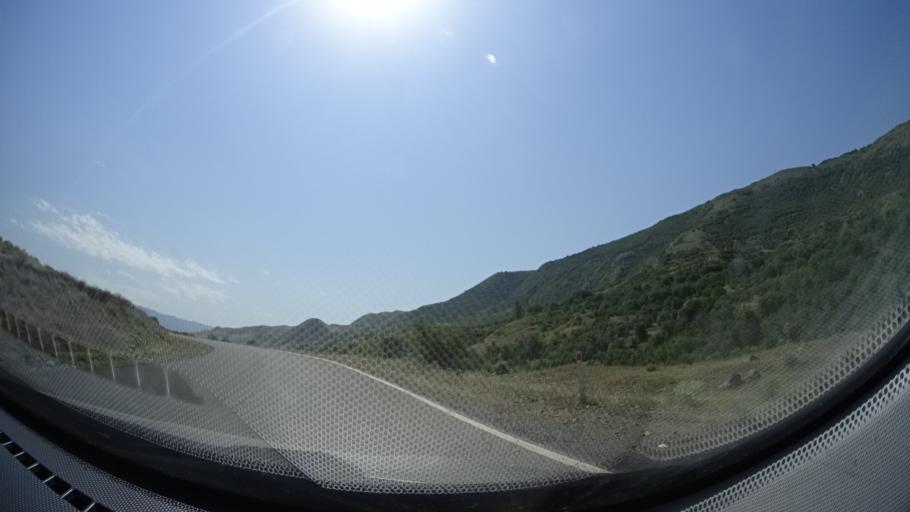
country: GE
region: Samtskhe-Javakheti
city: Aspindza
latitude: 41.5943
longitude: 43.1589
